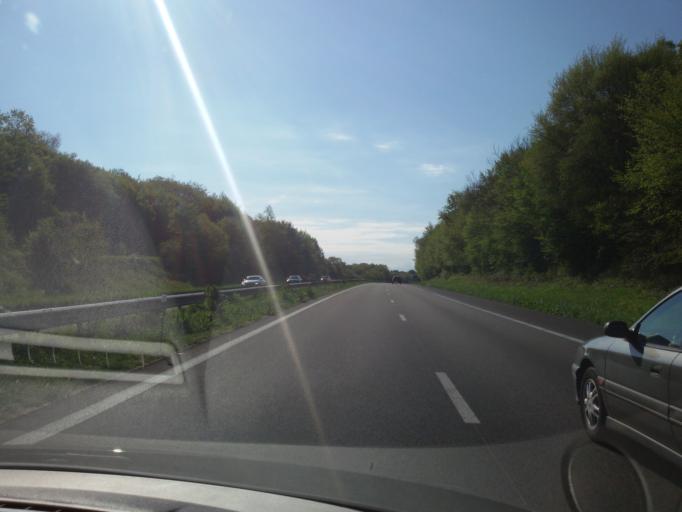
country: FR
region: Bourgogne
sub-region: Departement de l'Yonne
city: Joux-la-Ville
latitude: 47.6876
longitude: 3.8477
